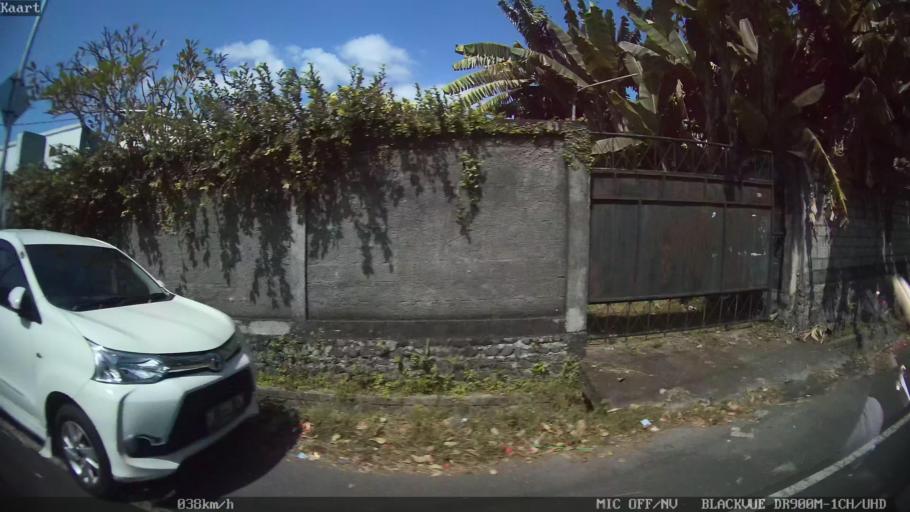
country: ID
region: Bali
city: Banjar Kertasari
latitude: -8.6417
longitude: 115.1751
